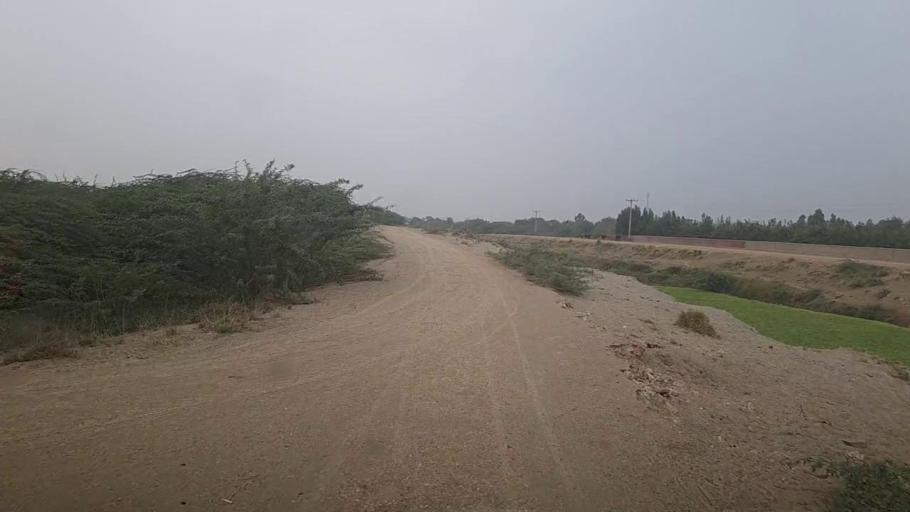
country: PK
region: Sindh
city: Gambat
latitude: 27.3600
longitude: 68.5695
